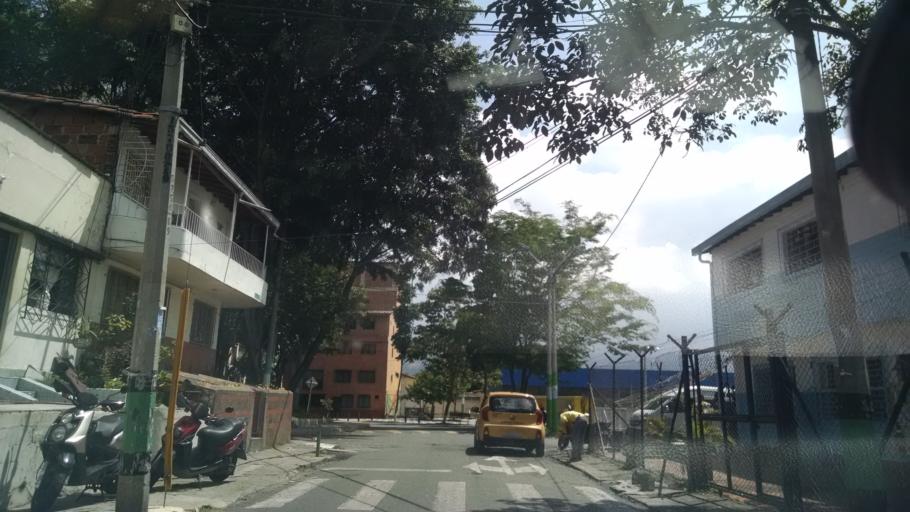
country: CO
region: Antioquia
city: Itagui
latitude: 6.2223
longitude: -75.5970
